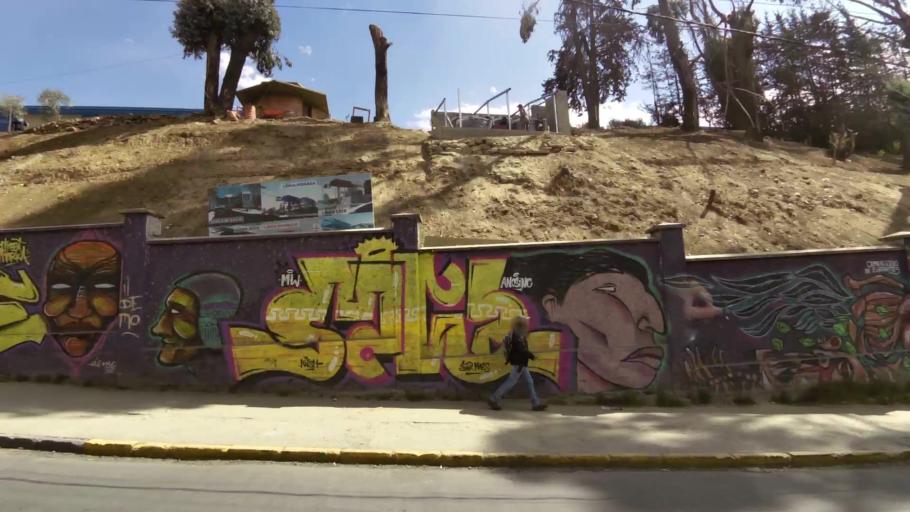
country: BO
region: La Paz
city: La Paz
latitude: -16.4897
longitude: -68.1447
